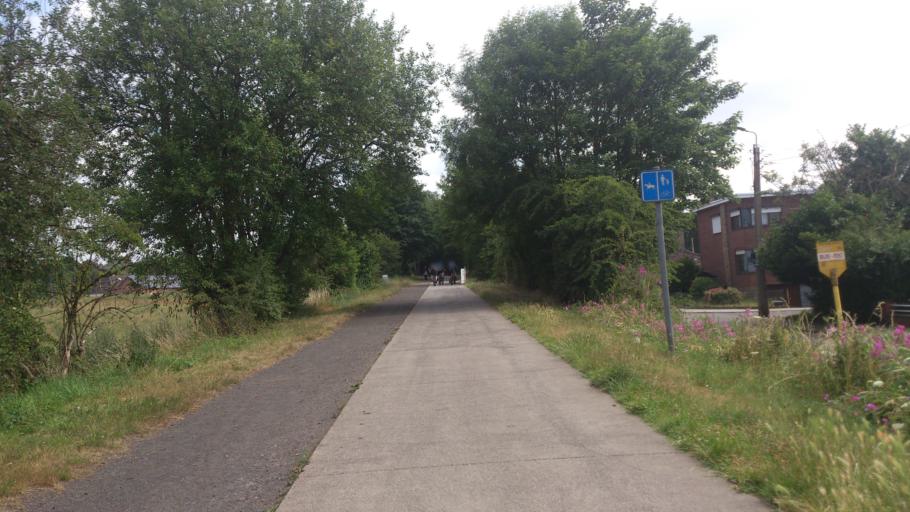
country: BE
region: Wallonia
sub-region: Province de Liege
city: Beyne-Heusay
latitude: 50.6298
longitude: 5.6335
